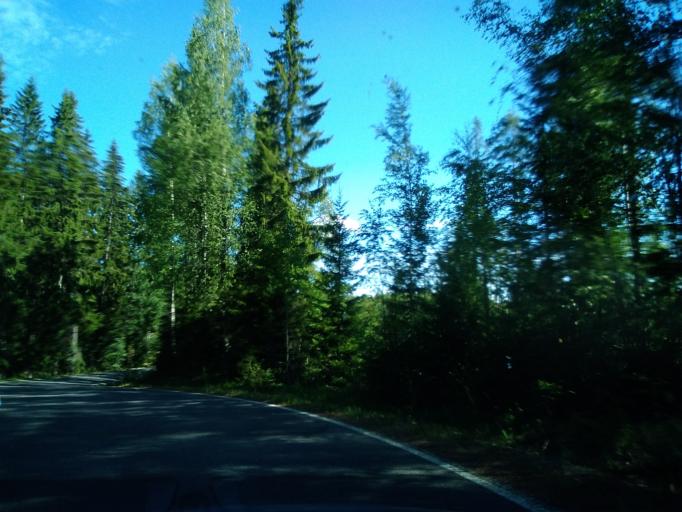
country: FI
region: Uusimaa
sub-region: Helsinki
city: Kaerkoelae
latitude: 60.7782
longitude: 24.0738
